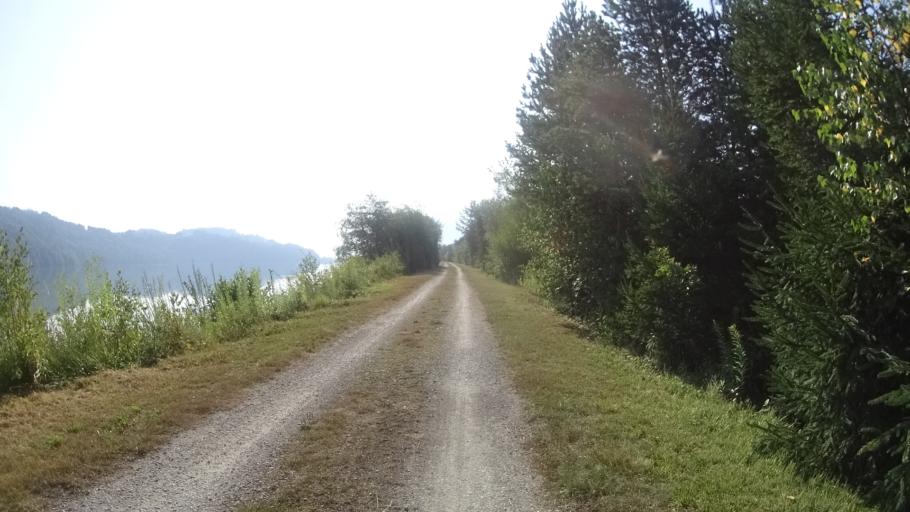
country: AT
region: Carinthia
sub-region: Politischer Bezirk Klagenfurt Land
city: Kottmannsdorf
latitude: 46.5438
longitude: 14.2281
